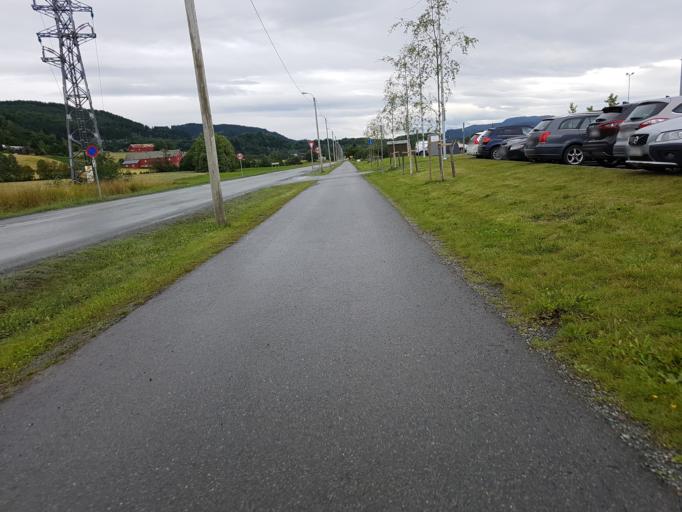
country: NO
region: Sor-Trondelag
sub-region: Trondheim
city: Trondheim
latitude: 63.3874
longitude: 10.4345
